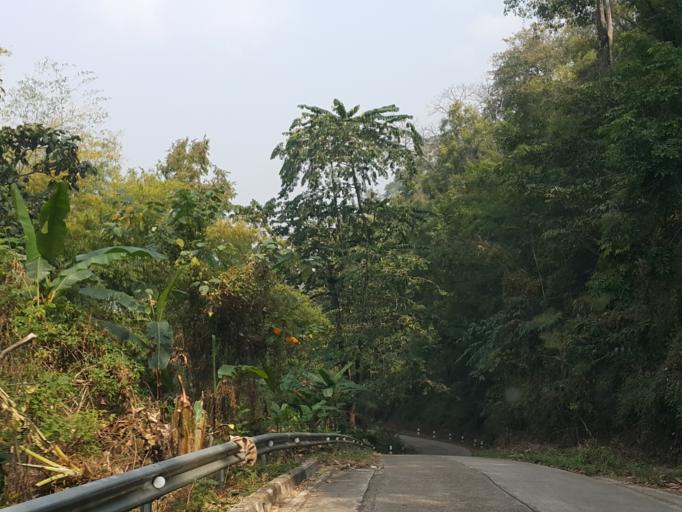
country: TH
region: Chiang Mai
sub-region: Amphoe Chiang Dao
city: Chiang Dao
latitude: 19.4120
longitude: 98.8642
